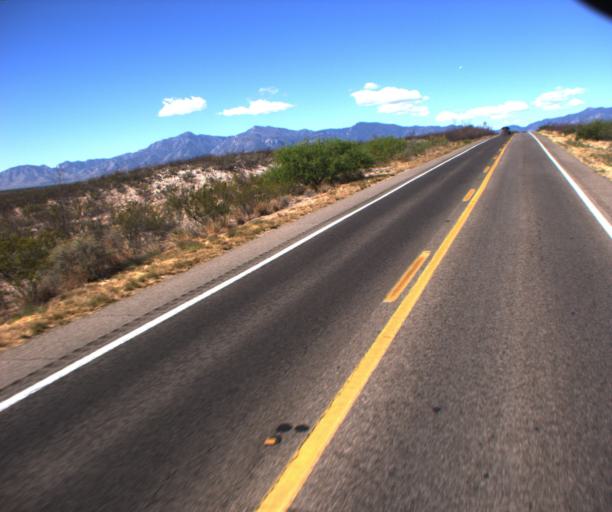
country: US
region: Arizona
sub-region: Cochise County
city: Sierra Vista Southeast
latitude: 31.5477
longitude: -110.1511
